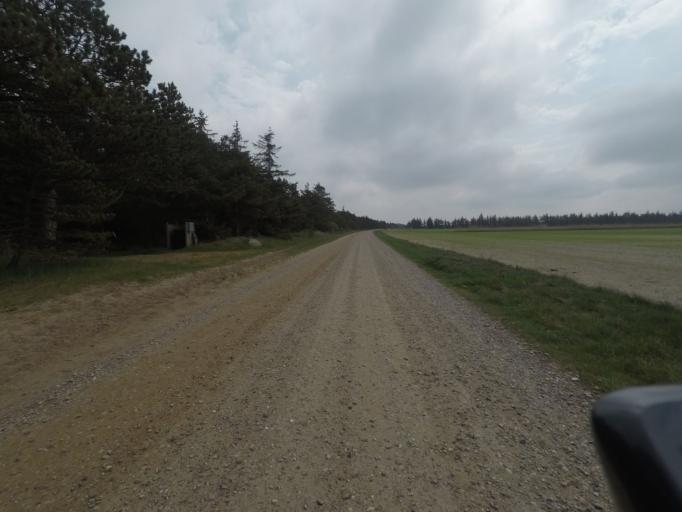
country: DE
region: Schleswig-Holstein
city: List
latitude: 55.0928
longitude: 8.5194
